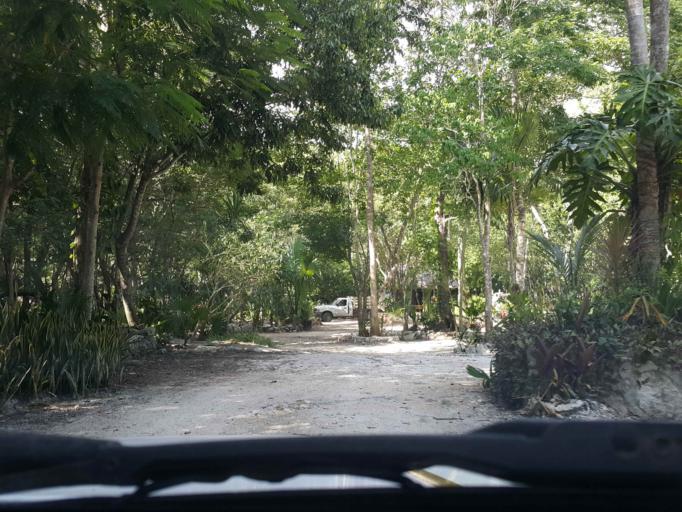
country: MX
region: Quintana Roo
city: Leona Vicario
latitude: 20.8756
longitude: -87.0437
